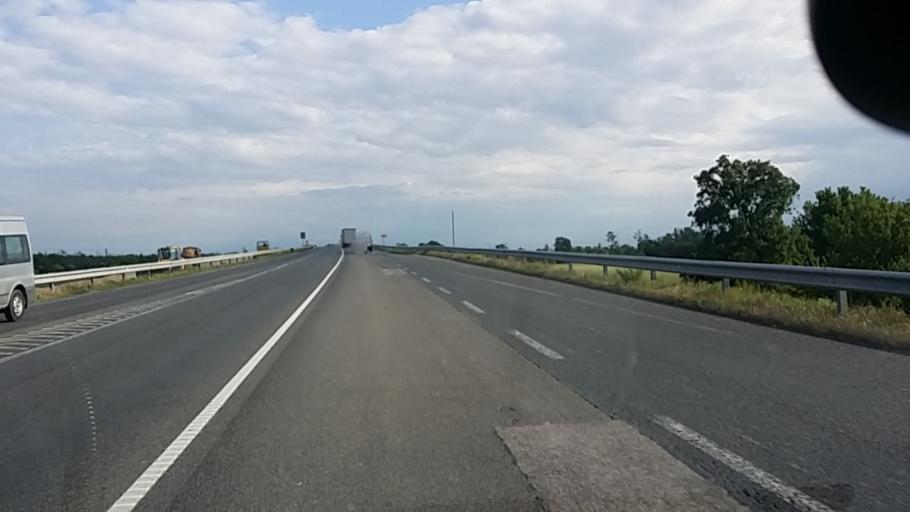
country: HU
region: Gyor-Moson-Sopron
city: Rajka
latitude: 47.9392
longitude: 17.1668
